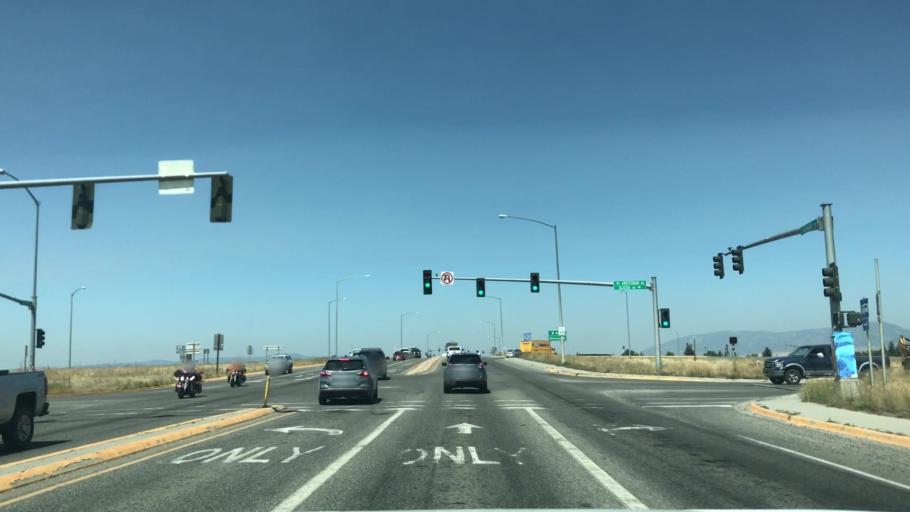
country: US
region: Montana
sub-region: Gallatin County
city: Belgrade
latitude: 45.7655
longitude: -111.1851
